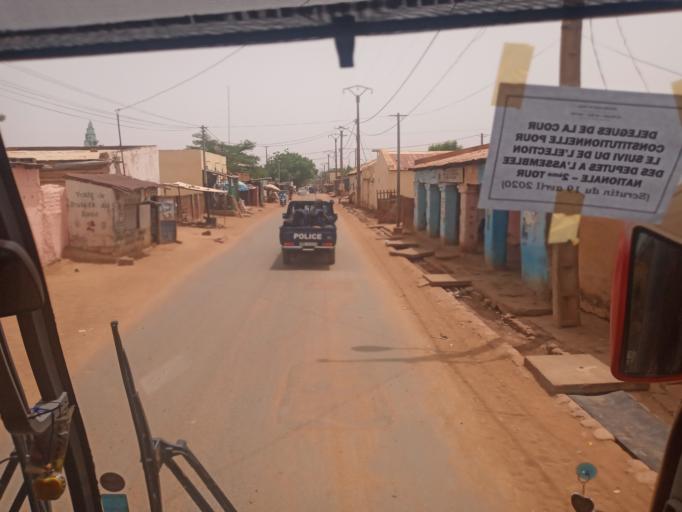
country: ML
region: Koulikoro
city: Koulikoro
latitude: 12.8906
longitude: -7.5411
